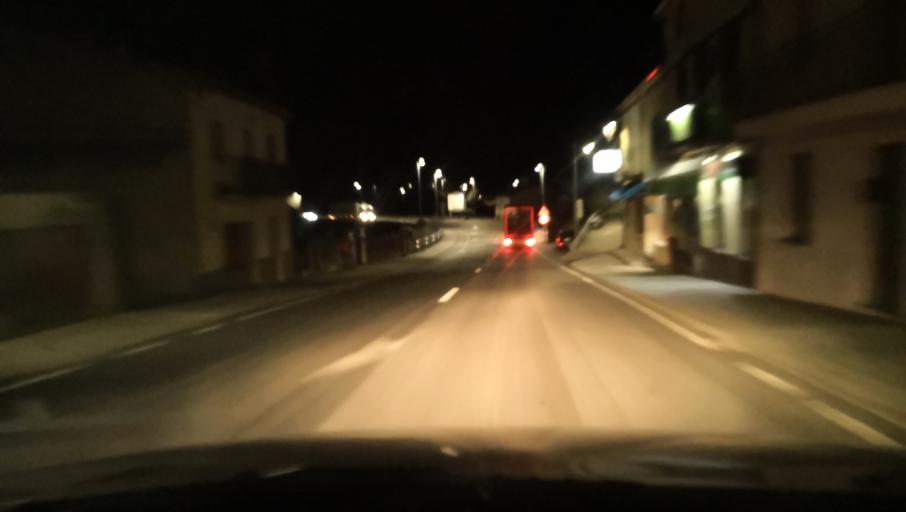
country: ES
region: Castille and Leon
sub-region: Provincia de Zamora
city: Alcanices
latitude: 41.6996
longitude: -6.3487
